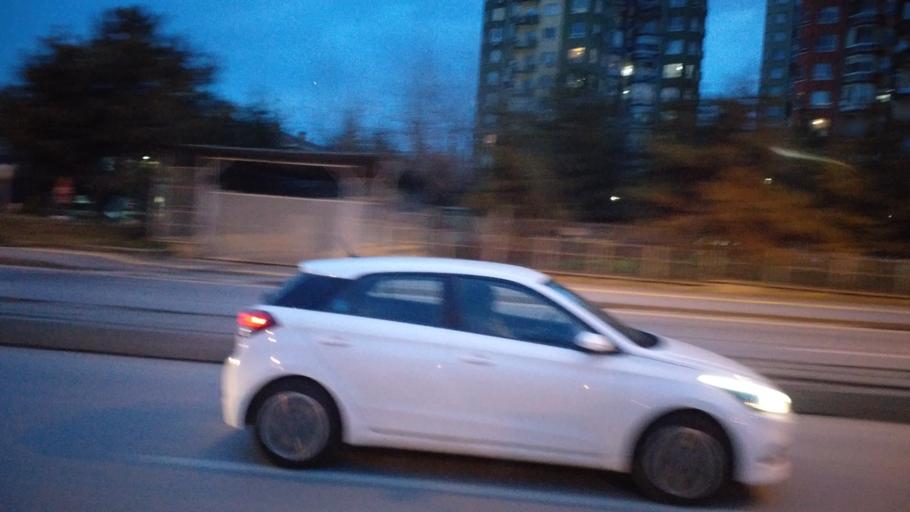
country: TR
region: Ankara
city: Ankara
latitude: 39.9689
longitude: 32.8331
